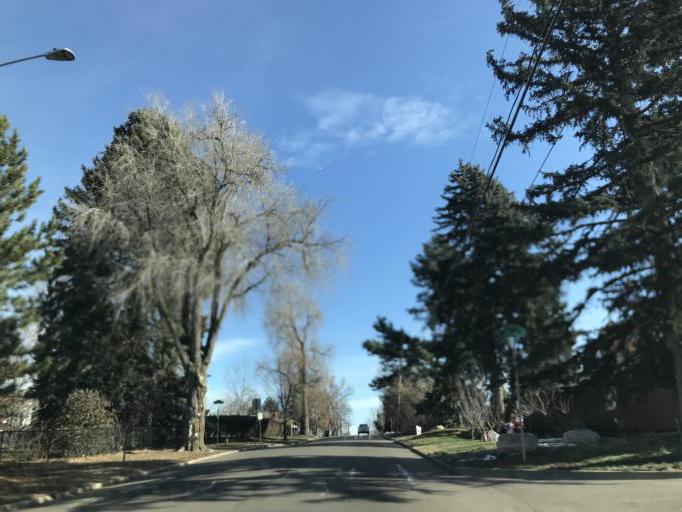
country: US
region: Colorado
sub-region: Arapahoe County
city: Glendale
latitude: 39.7356
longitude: -104.9076
